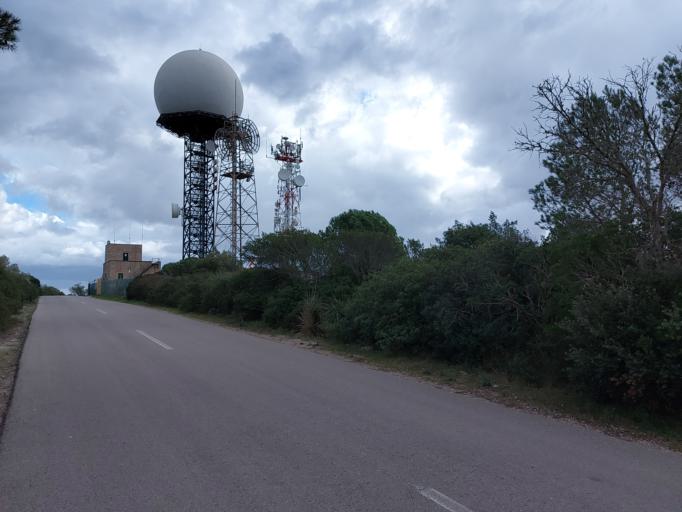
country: ES
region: Balearic Islands
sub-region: Illes Balears
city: Algaida
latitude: 39.5272
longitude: 2.9276
